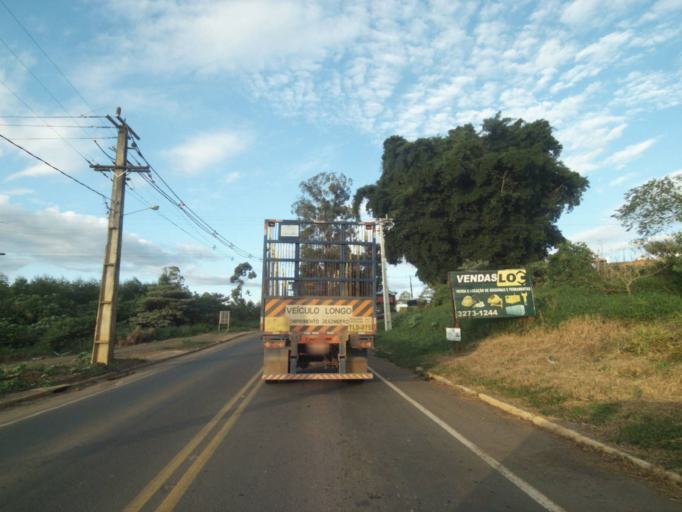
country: BR
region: Parana
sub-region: Telemaco Borba
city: Telemaco Borba
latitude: -24.3469
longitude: -50.6636
